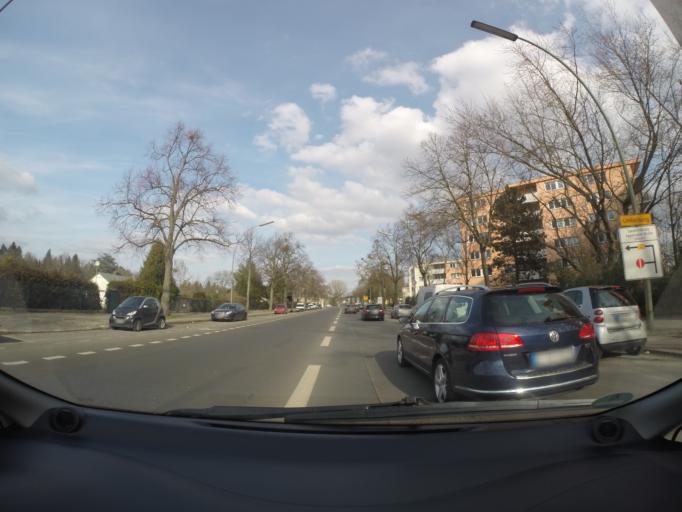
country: DE
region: Berlin
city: Lichterfelde
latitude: 52.4186
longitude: 13.2904
